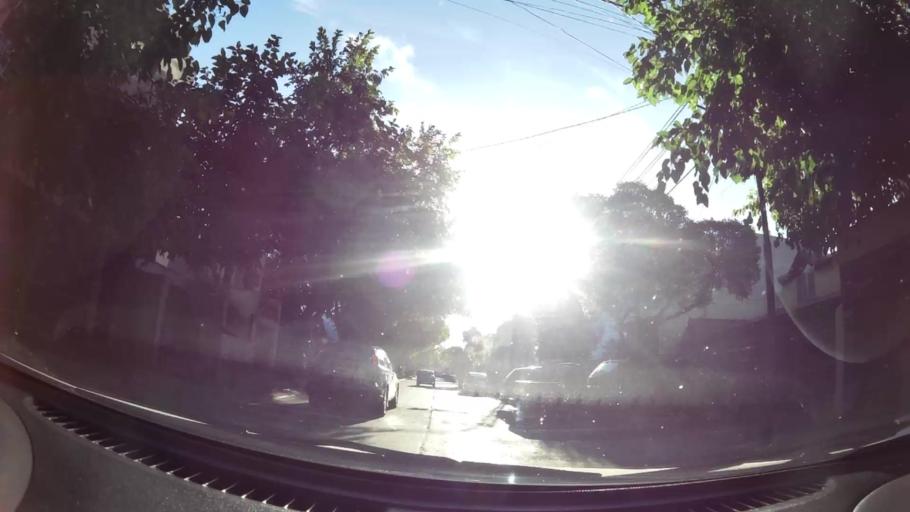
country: AR
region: Mendoza
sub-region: Departamento de Godoy Cruz
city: Godoy Cruz
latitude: -32.9076
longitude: -68.8497
